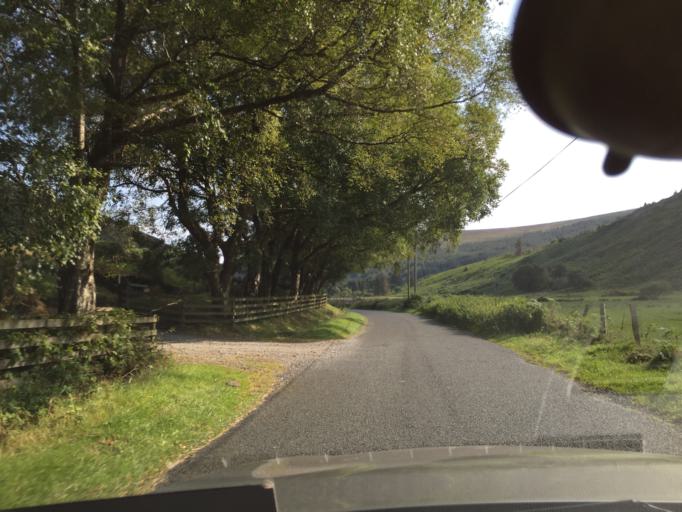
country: IE
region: Leinster
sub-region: Wicklow
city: Rathdrum
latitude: 53.0477
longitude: -6.3285
